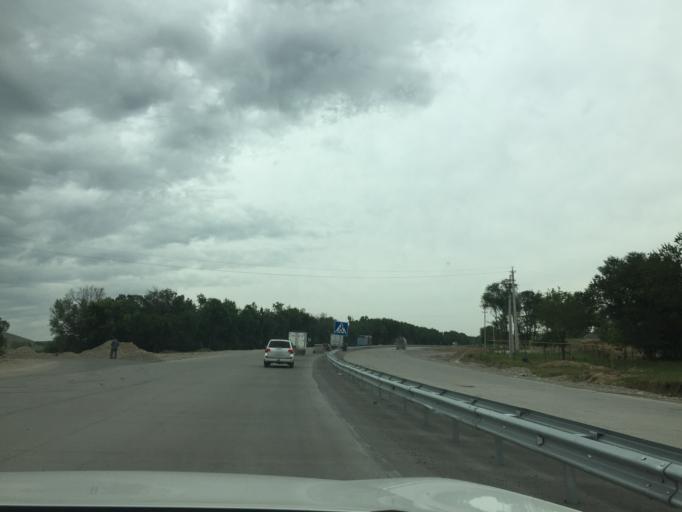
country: KZ
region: Ongtustik Qazaqstan
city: Sastobe
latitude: 42.5017
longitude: 69.9609
